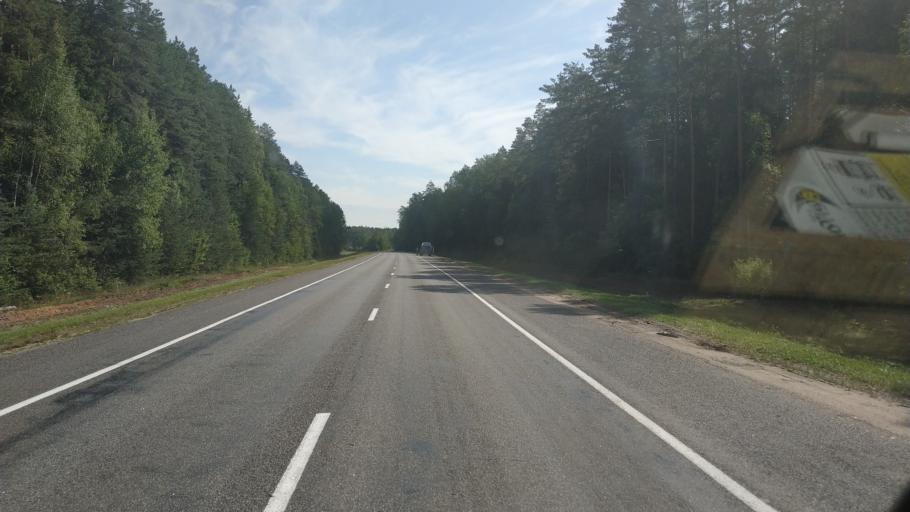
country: BY
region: Mogilev
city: Poselok Voskhod
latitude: 53.7736
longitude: 30.3812
